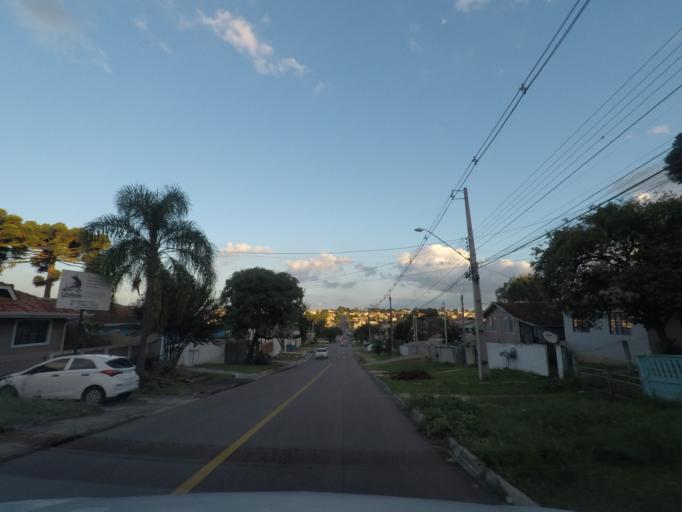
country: BR
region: Parana
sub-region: Sao Jose Dos Pinhais
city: Sao Jose dos Pinhais
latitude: -25.4946
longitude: -49.2576
